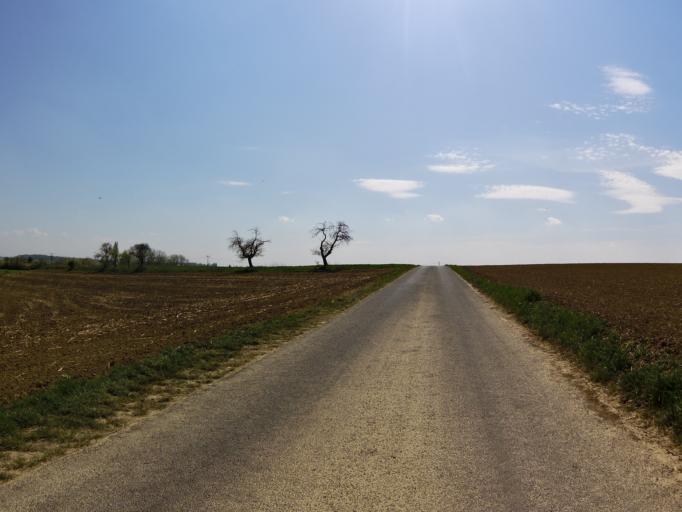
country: DE
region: Bavaria
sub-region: Regierungsbezirk Unterfranken
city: Giebelstadt
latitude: 49.6781
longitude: 9.9516
